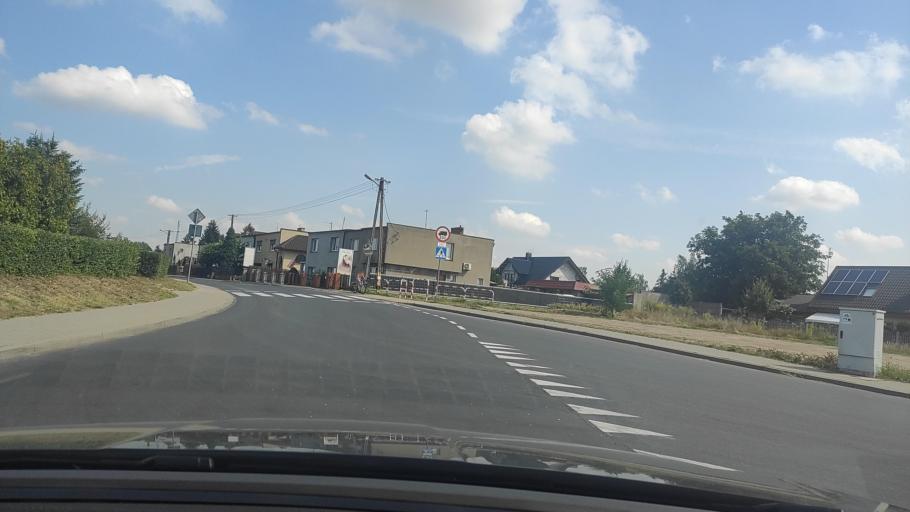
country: PL
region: Greater Poland Voivodeship
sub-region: Powiat poznanski
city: Kostrzyn
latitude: 52.4619
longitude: 17.1686
